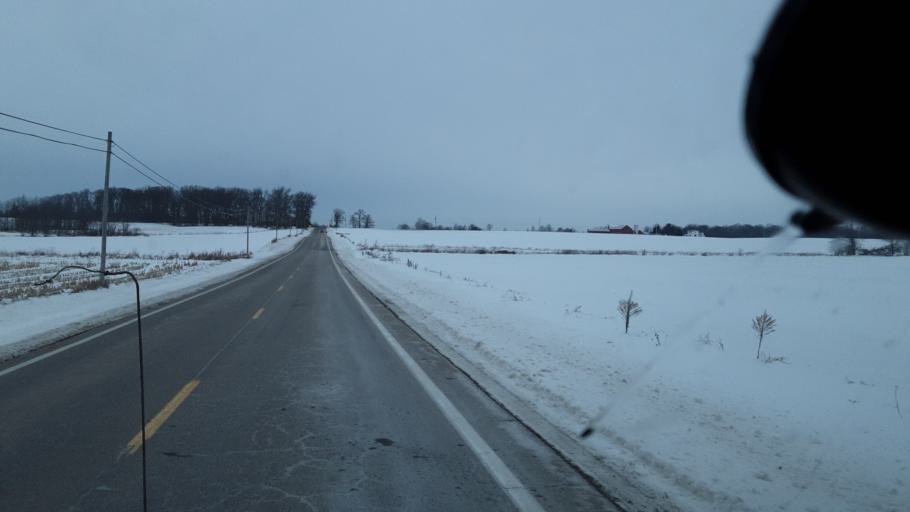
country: US
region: Ohio
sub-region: Union County
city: Marysville
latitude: 40.1797
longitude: -83.3353
